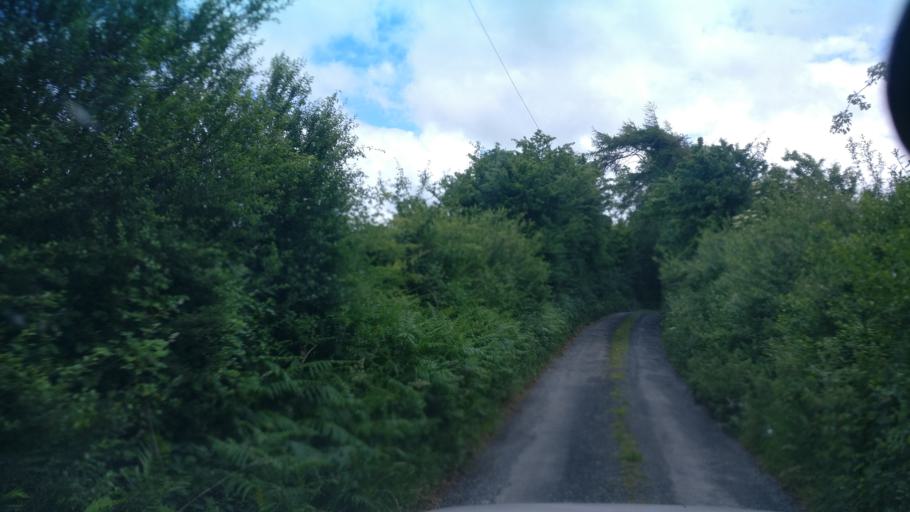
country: IE
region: Connaught
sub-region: County Galway
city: Loughrea
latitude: 53.1716
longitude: -8.5602
